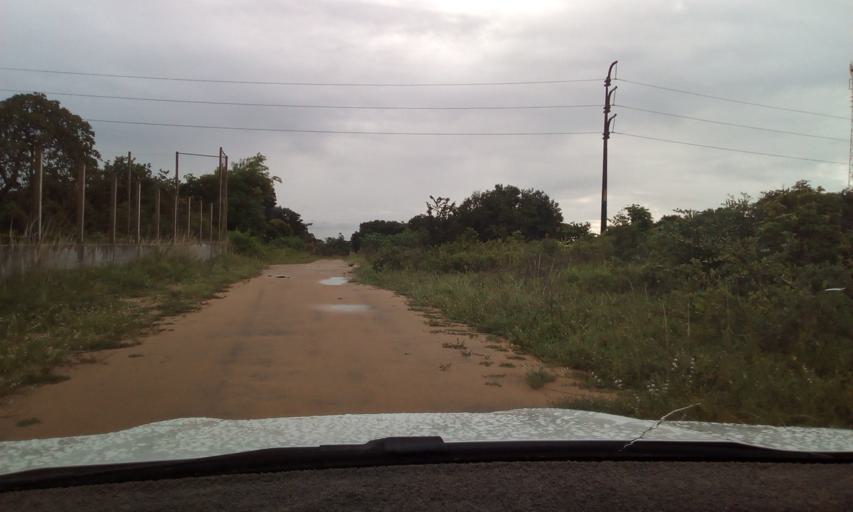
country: BR
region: Paraiba
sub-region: Joao Pessoa
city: Joao Pessoa
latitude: -7.1457
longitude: -34.8213
